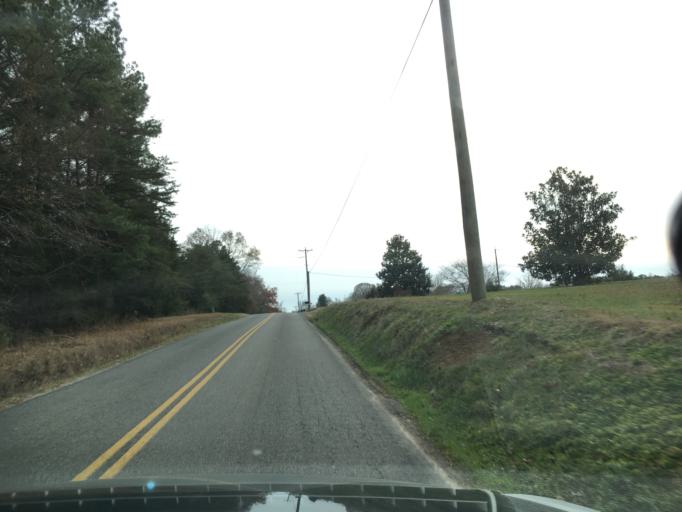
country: US
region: Virginia
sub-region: Henrico County
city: Wyndham
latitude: 37.7036
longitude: -77.6828
